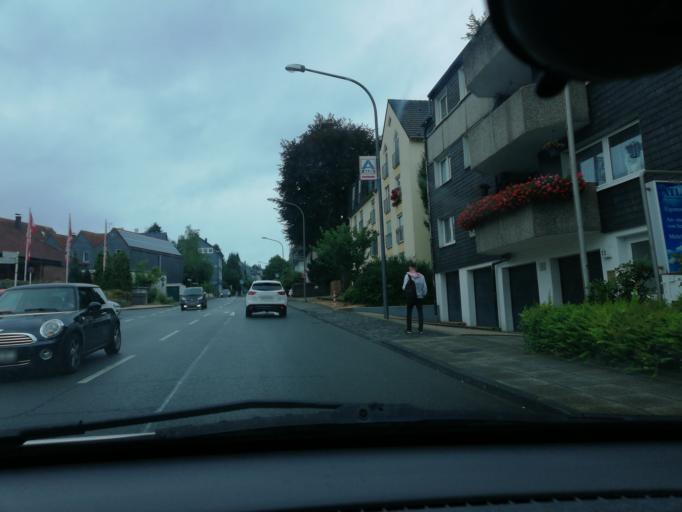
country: DE
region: North Rhine-Westphalia
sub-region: Regierungsbezirk Dusseldorf
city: Remscheid
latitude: 51.2274
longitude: 7.2039
